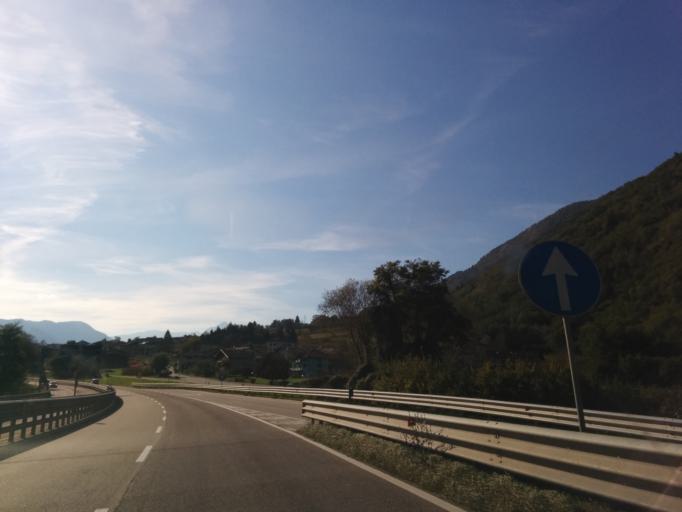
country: IT
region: Trentino-Alto Adige
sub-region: Provincia di Trento
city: Novaledo
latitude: 46.0285
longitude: 11.3766
